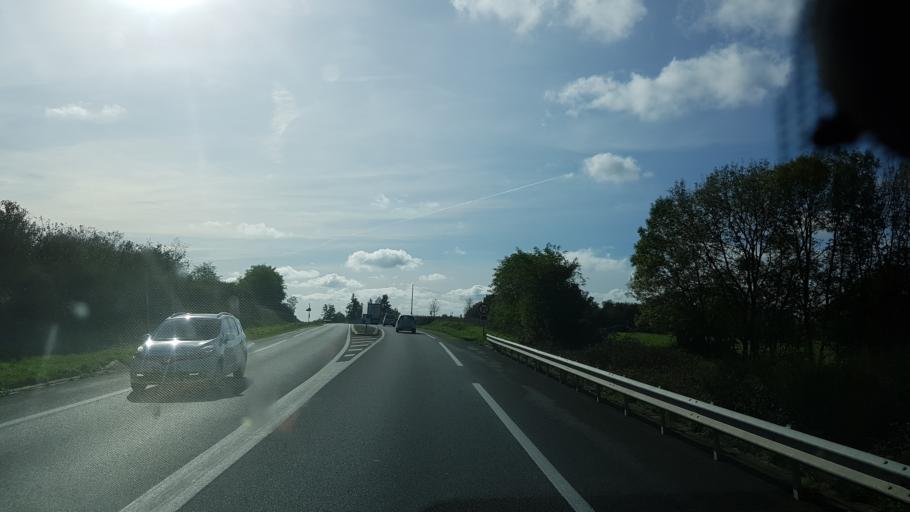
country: FR
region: Poitou-Charentes
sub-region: Departement de la Charente
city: Saint-Claud
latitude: 45.9082
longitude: 0.4890
